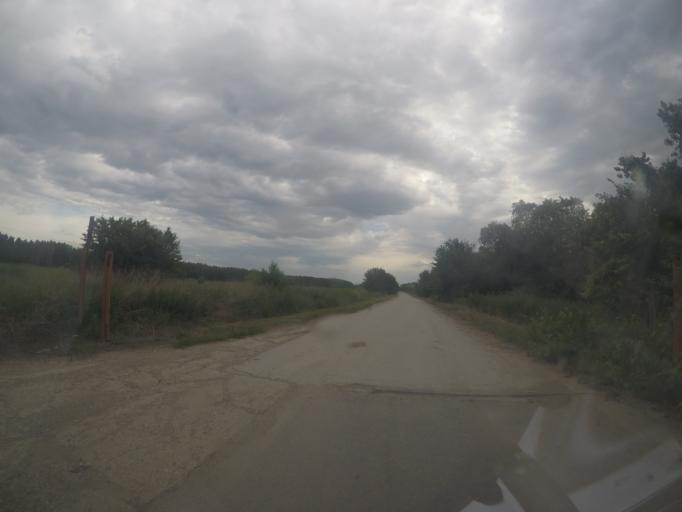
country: RS
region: Central Serbia
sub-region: Belgrade
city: Zemun
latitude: 44.8870
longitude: 20.3828
